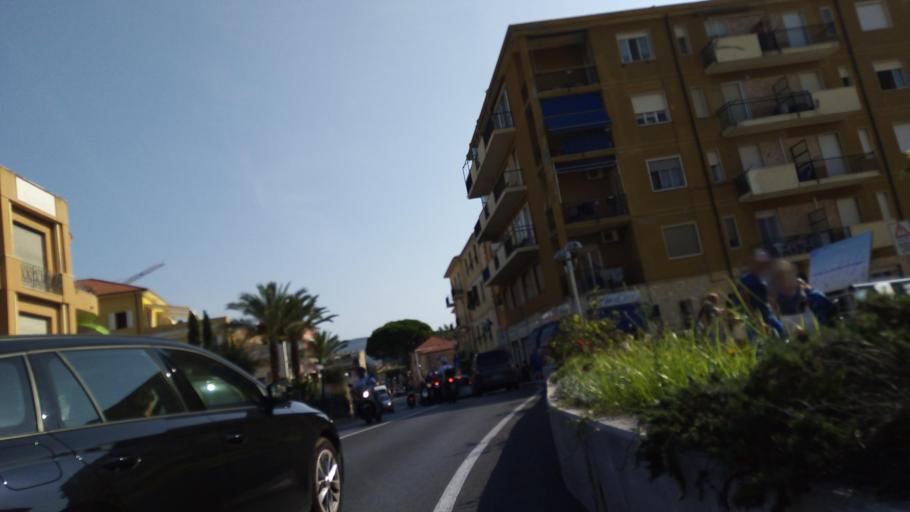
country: IT
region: Liguria
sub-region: Provincia di Savona
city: Pietra Ligure
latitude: 44.1444
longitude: 8.2752
